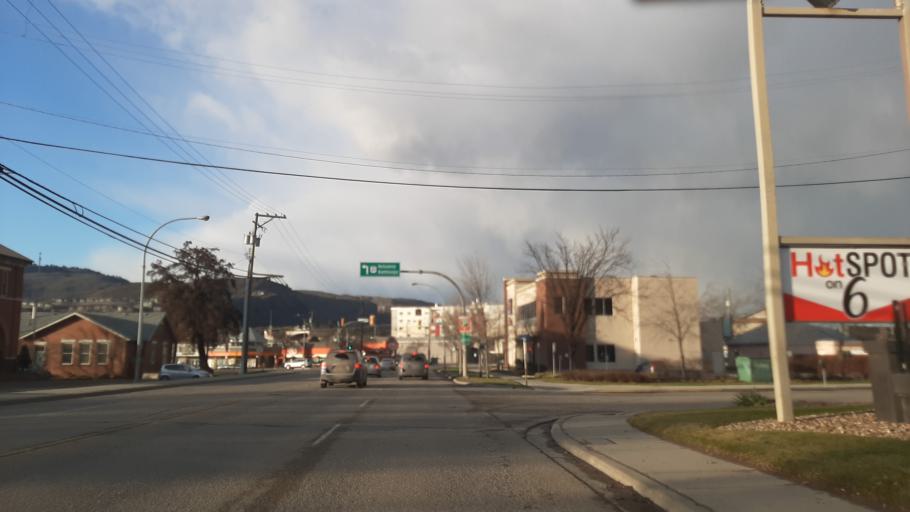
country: CA
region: British Columbia
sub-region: Regional District of North Okanagan
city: Vernon
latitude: 50.2604
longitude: -119.2698
